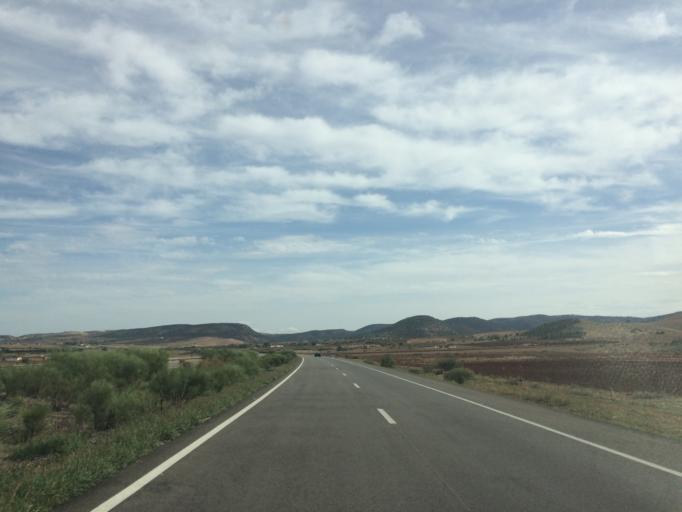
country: MA
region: Rabat-Sale-Zemmour-Zaer
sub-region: Khemisset
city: Khemisset
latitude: 33.7837
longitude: -5.9117
